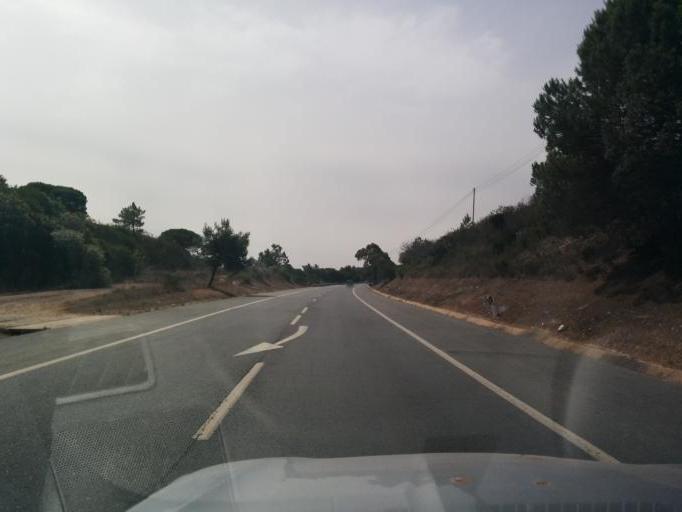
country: PT
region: Beja
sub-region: Odemira
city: Vila Nova de Milfontes
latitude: 37.7239
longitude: -8.7685
